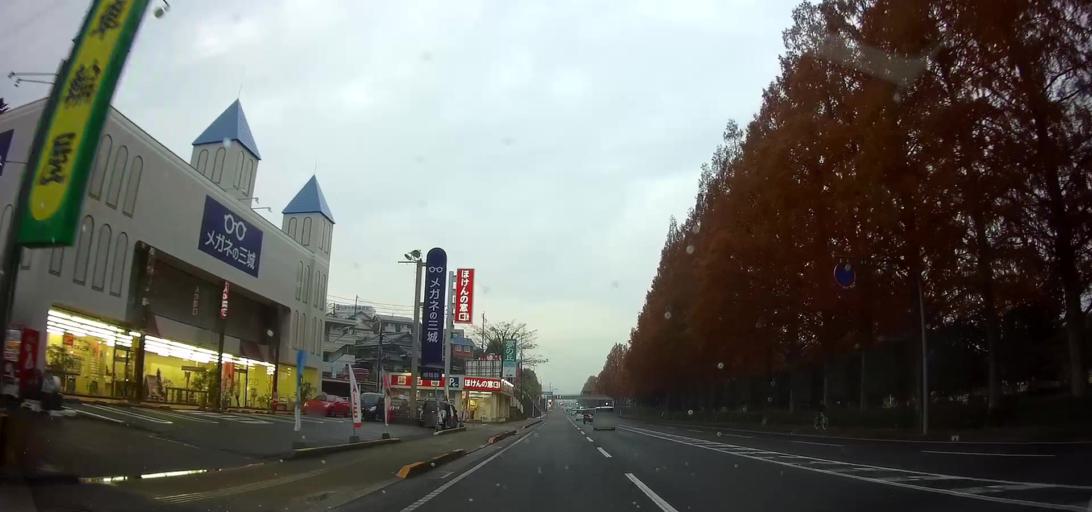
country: JP
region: Nagasaki
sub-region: Isahaya-shi
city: Isahaya
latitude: 32.8355
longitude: 130.0401
